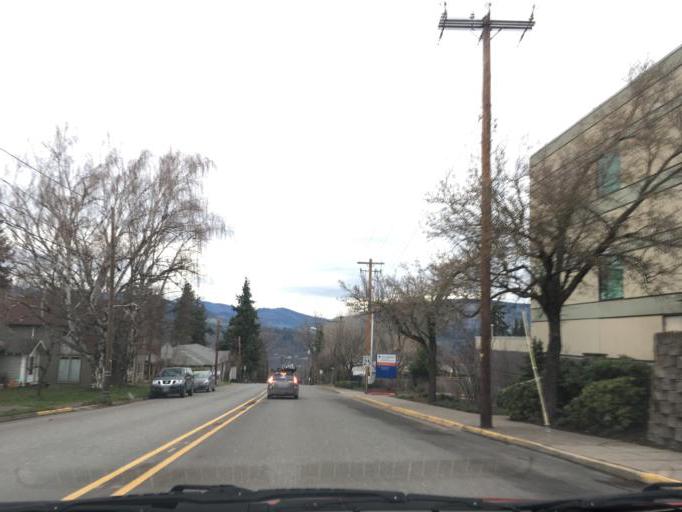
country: US
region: Oregon
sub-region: Hood River County
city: Hood River
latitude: 45.7046
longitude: -121.5251
